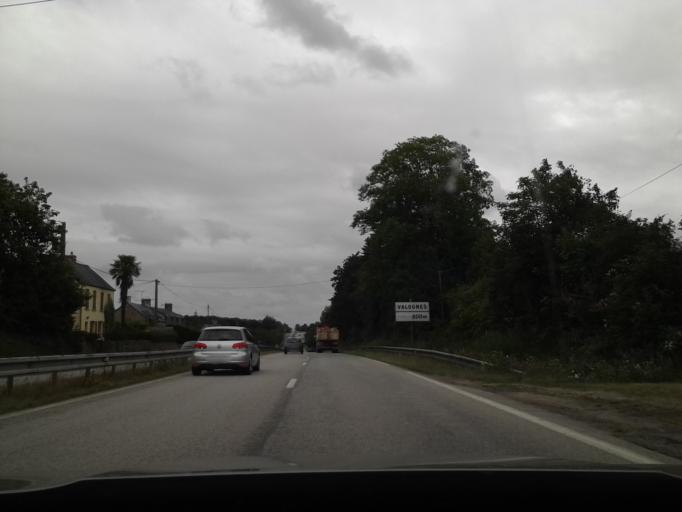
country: FR
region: Lower Normandy
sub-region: Departement de la Manche
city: Valognes
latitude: 49.5267
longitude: -1.5127
